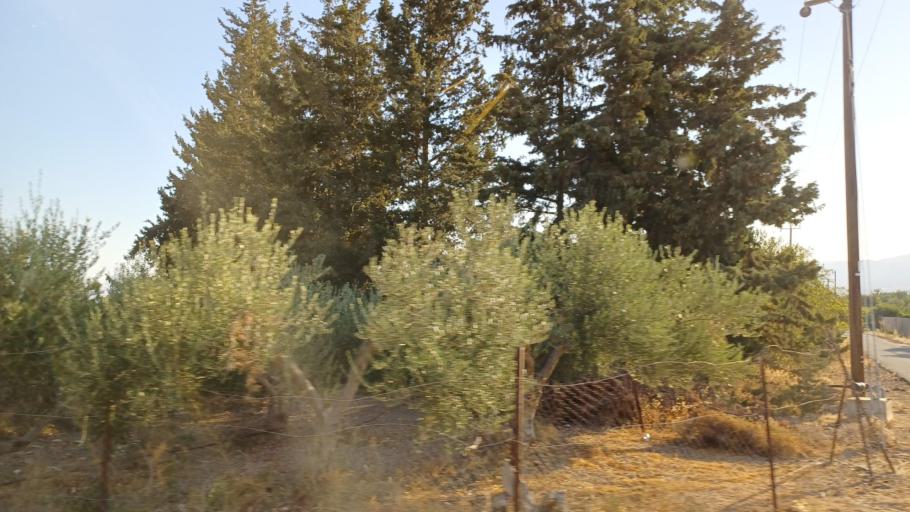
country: CY
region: Pafos
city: Polis
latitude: 35.0263
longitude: 32.3880
